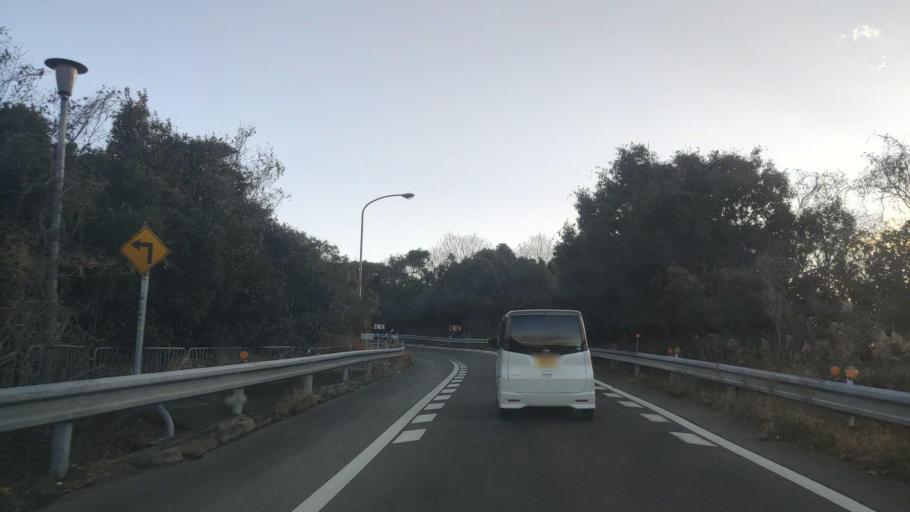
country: JP
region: Hyogo
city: Tatsunocho-tominaga
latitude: 34.8474
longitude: 134.6035
